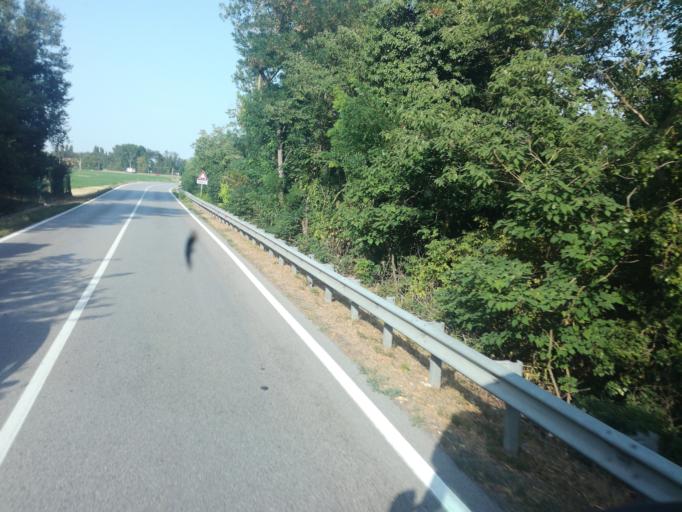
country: IT
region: Emilia-Romagna
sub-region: Provincia di Bologna
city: Progresso
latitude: 44.5496
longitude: 11.3838
